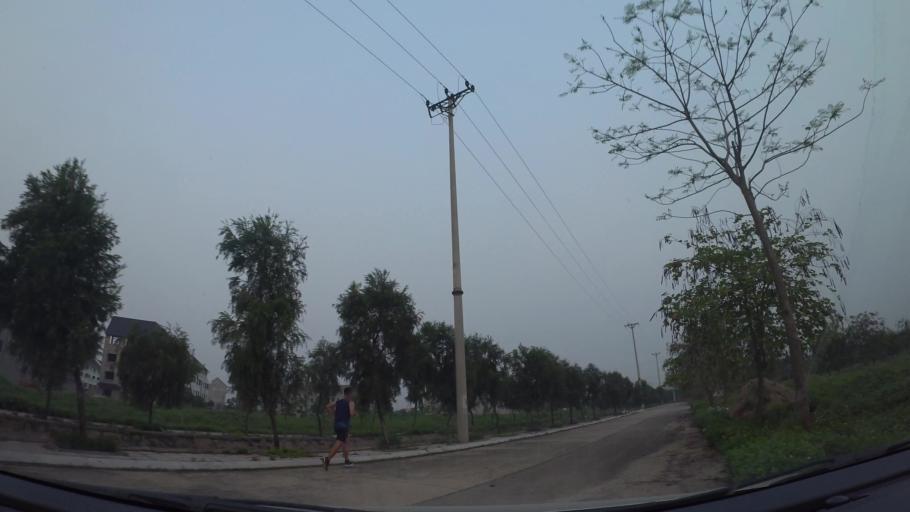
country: VN
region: Ha Noi
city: Ha Dong
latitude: 20.9950
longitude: 105.7326
